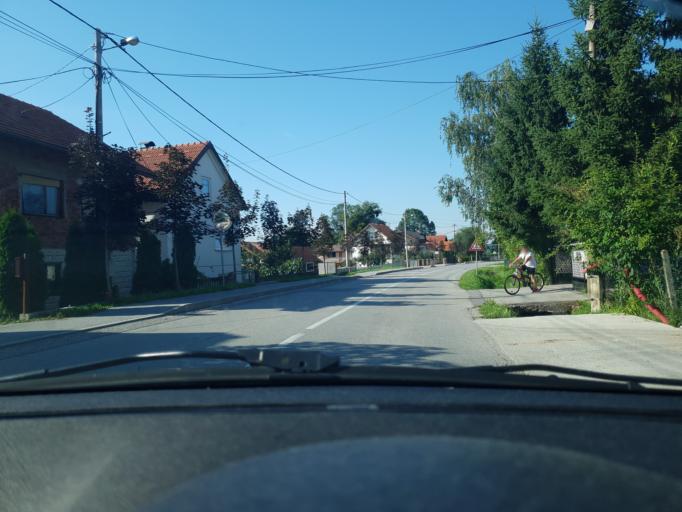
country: HR
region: Zagrebacka
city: Jablanovec
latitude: 45.8910
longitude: 15.8566
